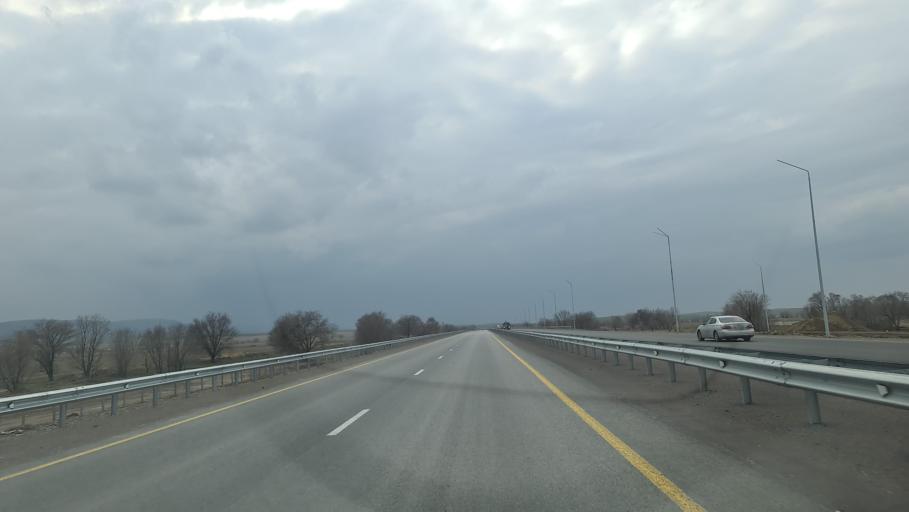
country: KG
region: Chuy
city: Bystrovka
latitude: 43.3204
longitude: 76.0274
